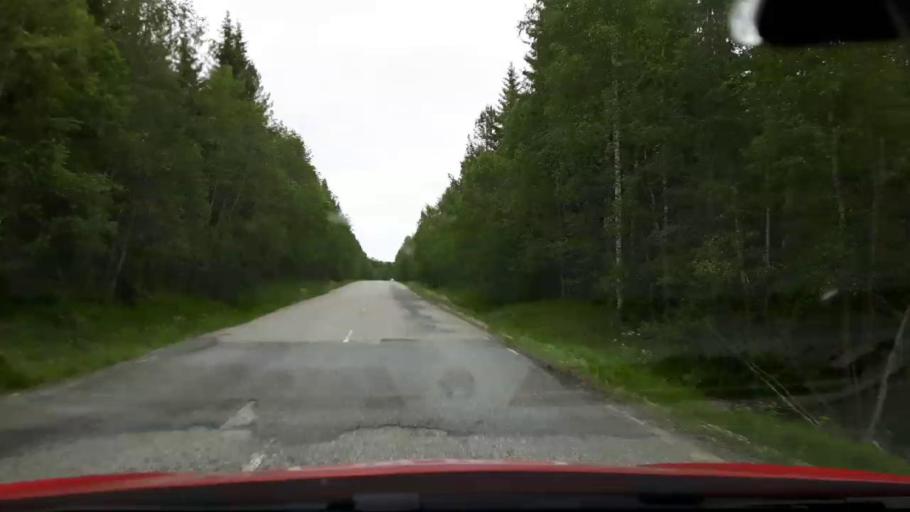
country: SE
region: Jaemtland
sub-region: Ragunda Kommun
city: Hammarstrand
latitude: 63.2361
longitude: 15.9191
